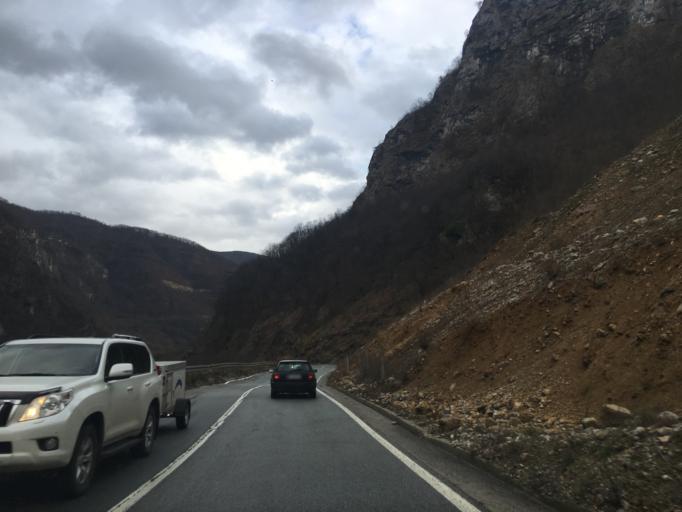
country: RS
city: Sokolovo Brdo
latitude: 43.1610
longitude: 19.7722
